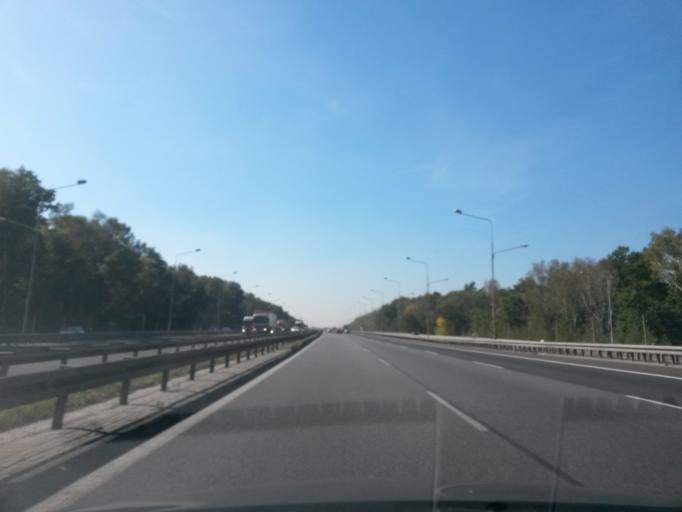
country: PL
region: Silesian Voivodeship
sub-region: Chorzow
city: Chorzow
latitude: 50.2560
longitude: 18.9625
